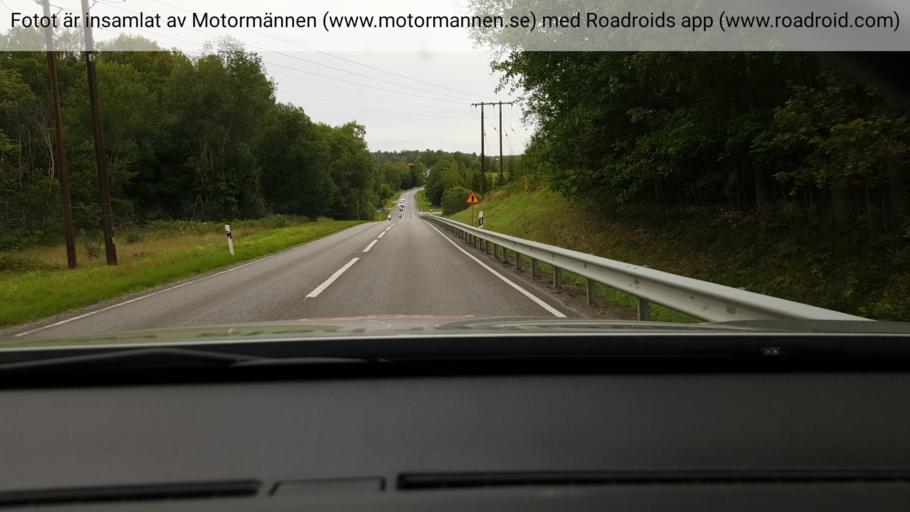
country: SE
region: Stockholm
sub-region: Sodertalje Kommun
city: Molnbo
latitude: 59.0425
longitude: 17.3944
